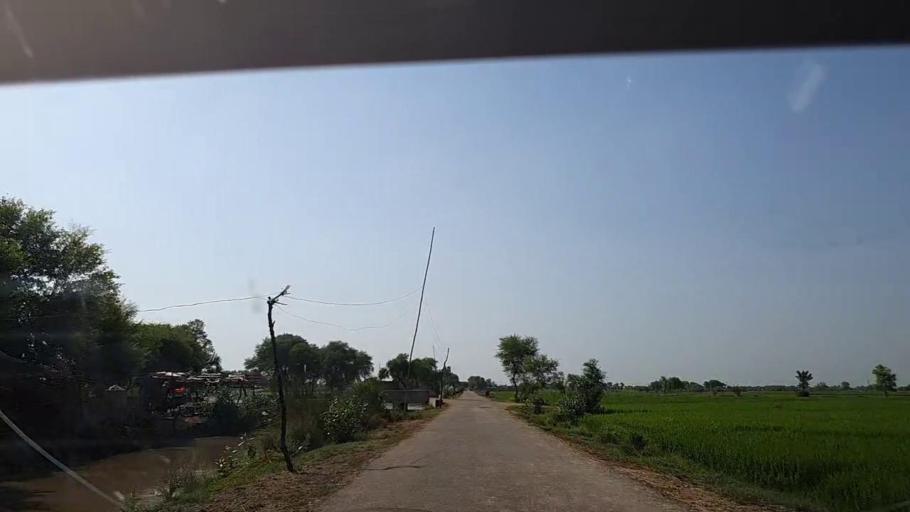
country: PK
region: Sindh
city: Tangwani
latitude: 28.2074
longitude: 69.0294
